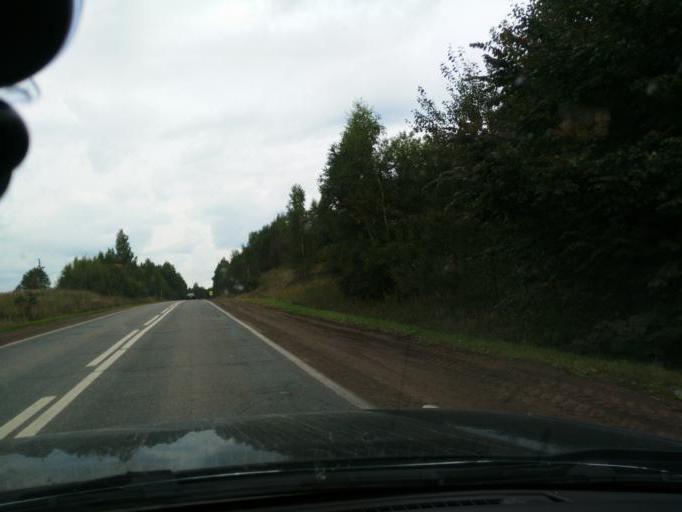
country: RU
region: Perm
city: Chernushka
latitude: 56.6730
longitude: 56.1702
